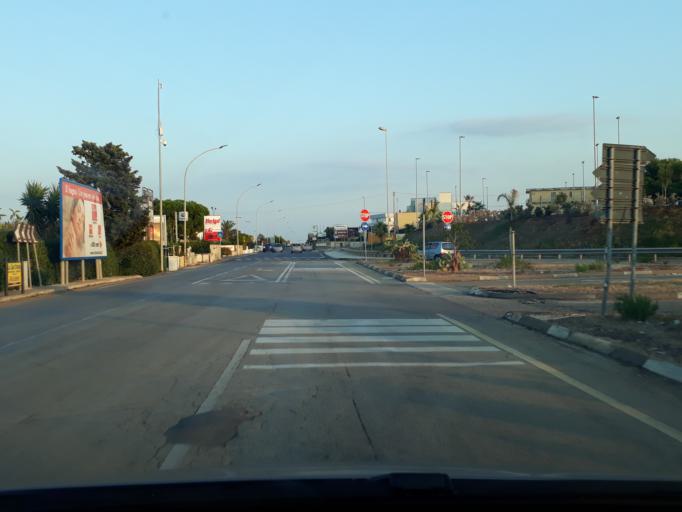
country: IT
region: Apulia
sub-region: Provincia di Bari
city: Monopoli
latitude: 40.9714
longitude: 17.2634
